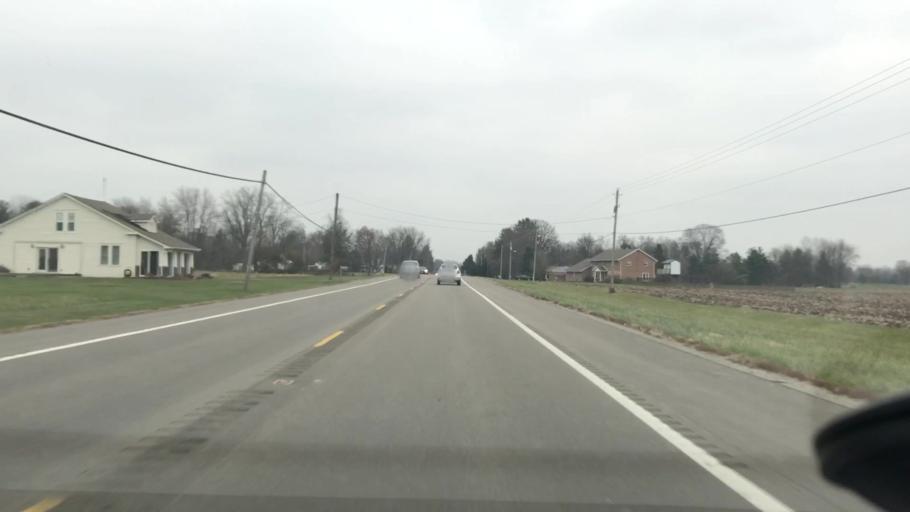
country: US
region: Ohio
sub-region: Greene County
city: Yellow Springs
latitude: 39.8584
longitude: -83.8521
